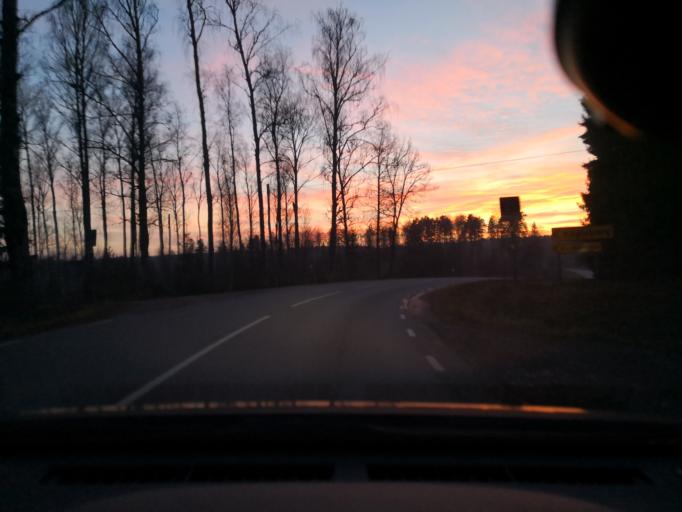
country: SE
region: OErebro
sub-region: Lindesbergs Kommun
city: Fellingsbro
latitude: 59.4037
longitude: 15.5299
